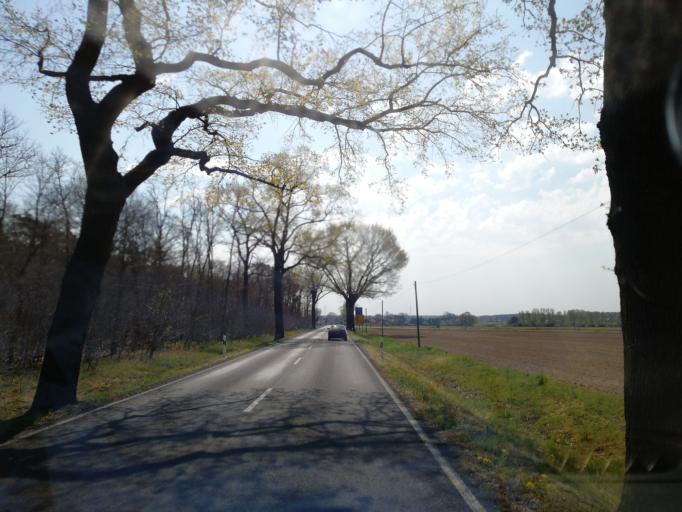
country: DE
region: Brandenburg
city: Calau
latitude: 51.7673
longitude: 13.9035
